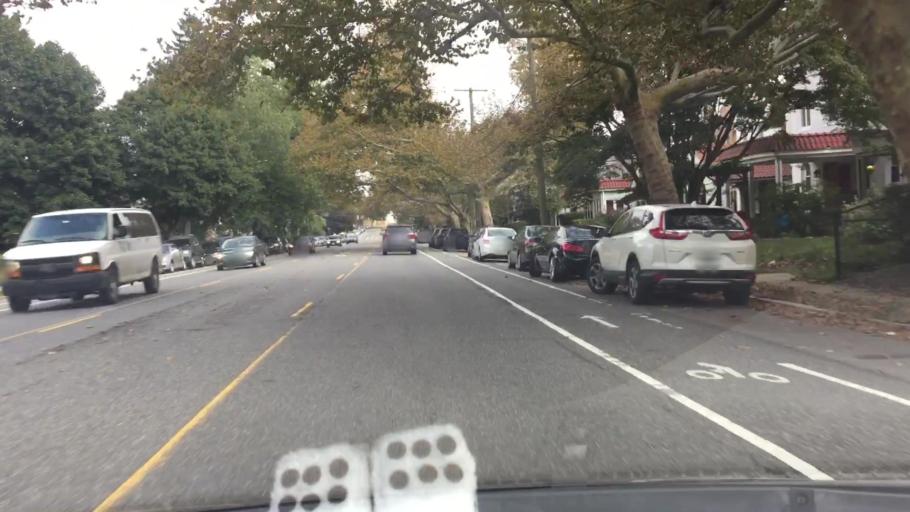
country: US
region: Pennsylvania
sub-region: Montgomery County
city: Bala-Cynwyd
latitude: 40.0003
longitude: -75.2244
